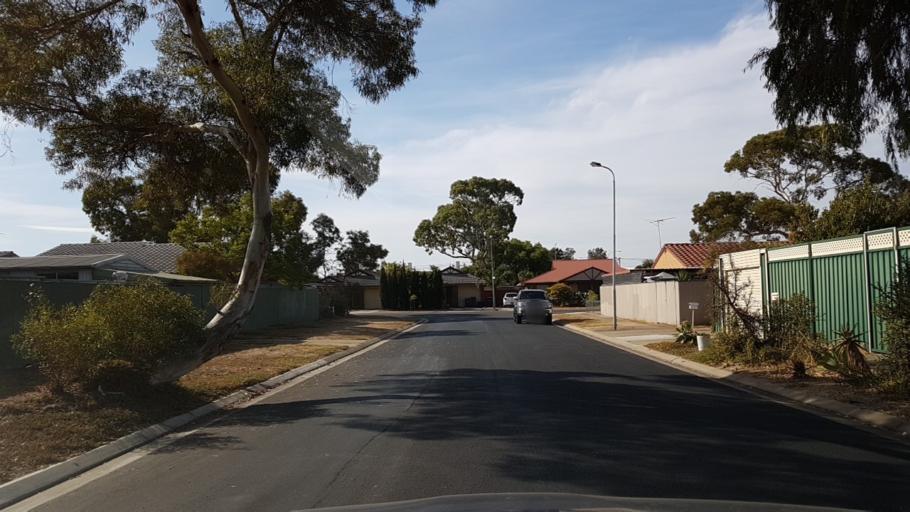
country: AU
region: South Australia
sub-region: Charles Sturt
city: West Lakes Shore
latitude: -34.8534
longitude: 138.4944
